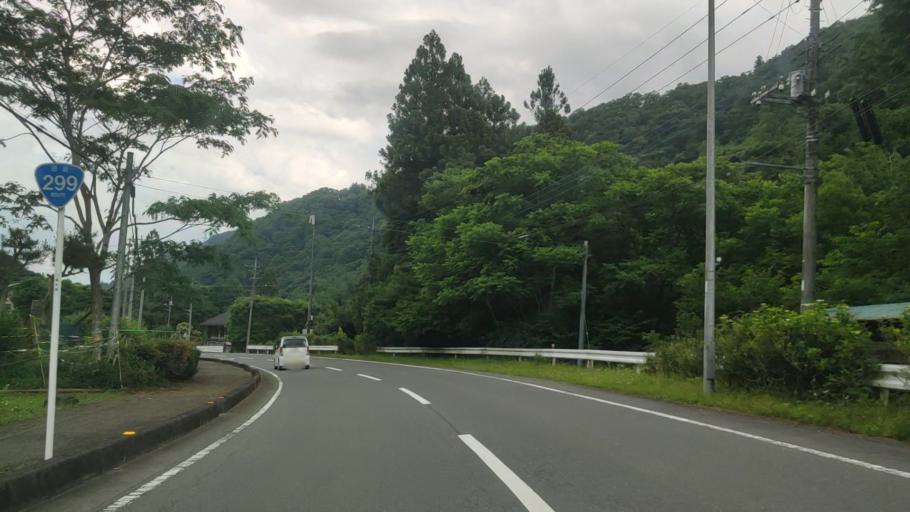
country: JP
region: Saitama
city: Chichibu
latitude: 36.0369
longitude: 138.9152
